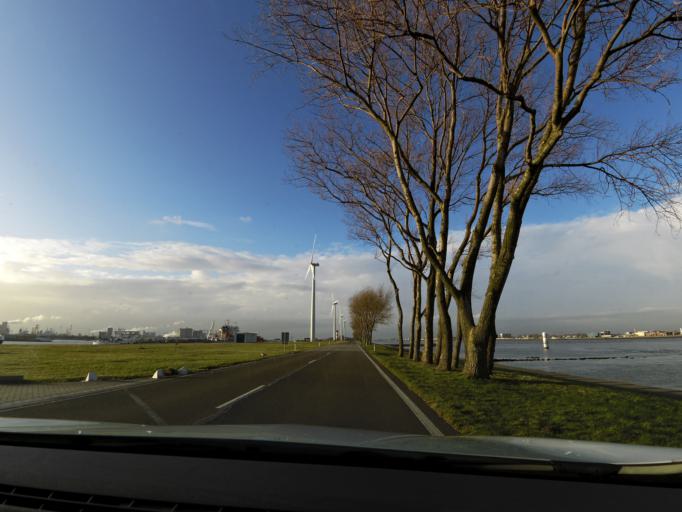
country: NL
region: South Holland
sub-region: Gemeente Rotterdam
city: Hoek van Holland
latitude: 51.9547
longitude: 4.1558
